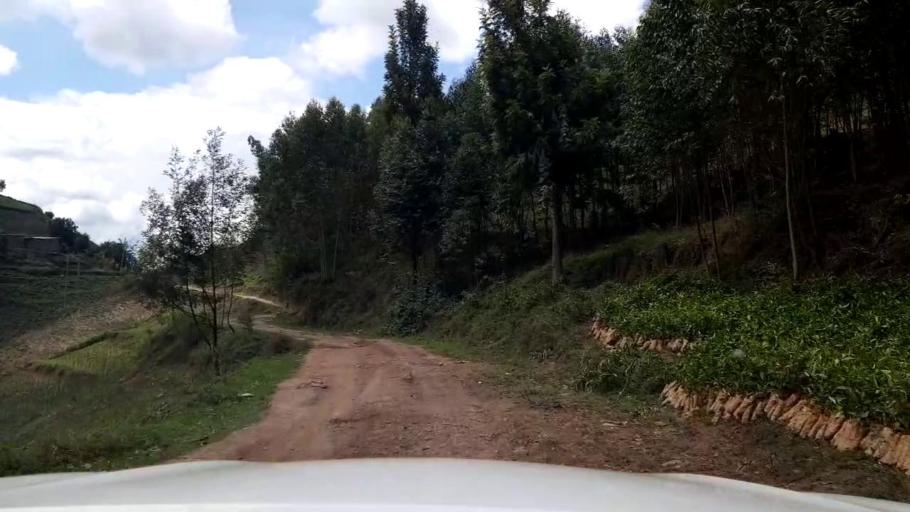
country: RW
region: Northern Province
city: Byumba
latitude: -1.5200
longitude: 30.1284
